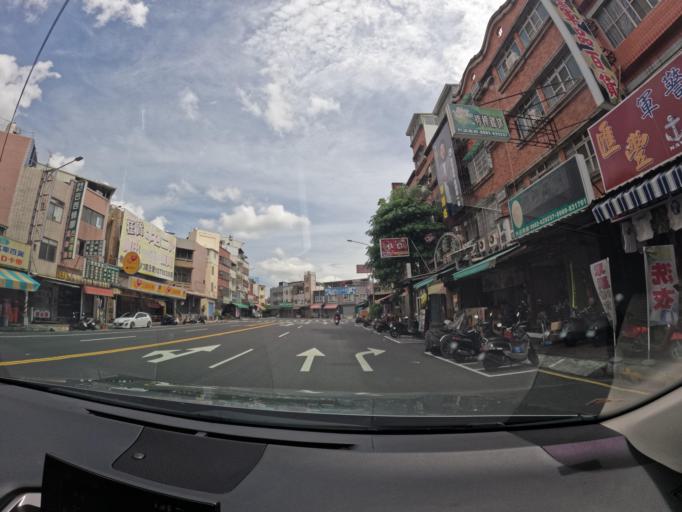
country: TW
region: Kaohsiung
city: Kaohsiung
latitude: 22.6892
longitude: 120.2923
